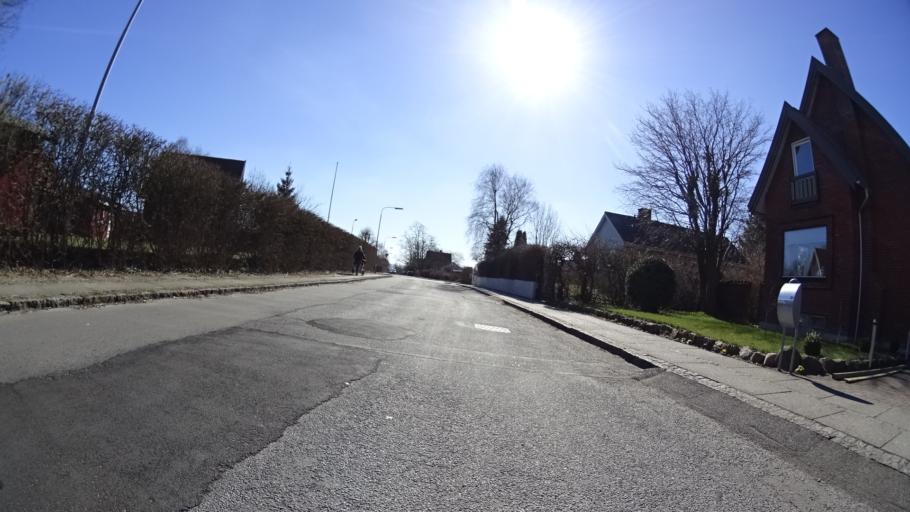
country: DK
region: Central Jutland
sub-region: Arhus Kommune
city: Arhus
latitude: 56.1707
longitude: 10.1659
